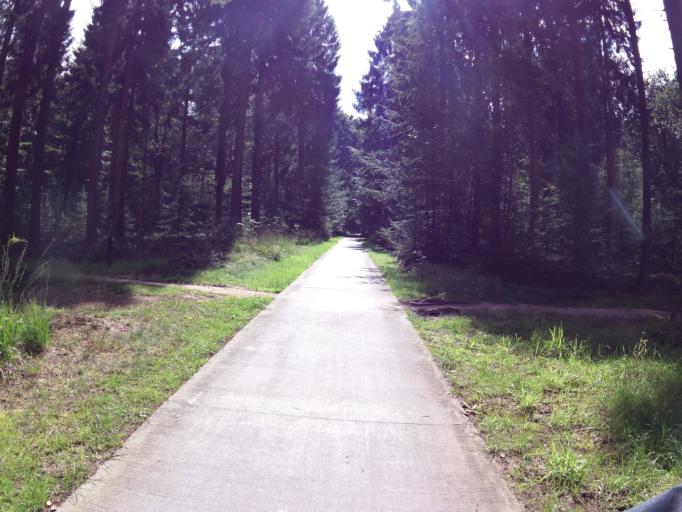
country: NL
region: Drenthe
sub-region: Gemeente Borger-Odoorn
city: Borger
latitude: 52.9487
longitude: 6.7514
